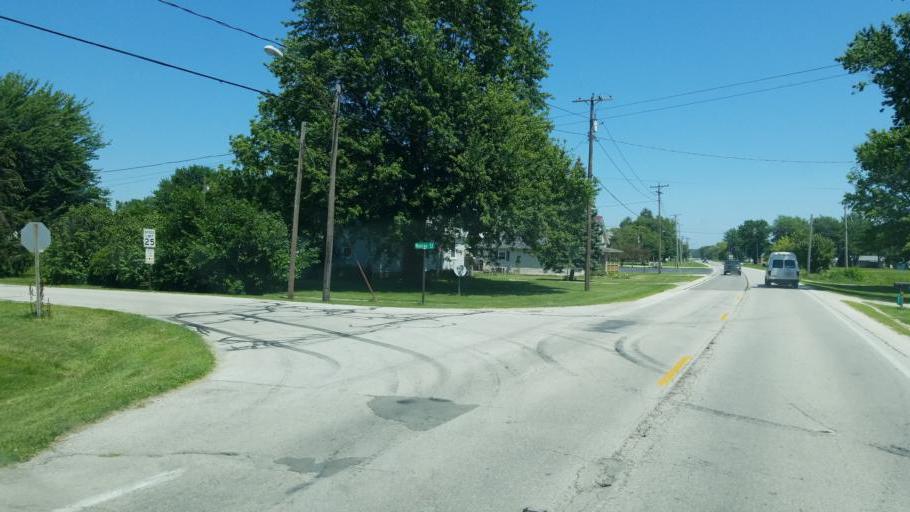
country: US
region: Ohio
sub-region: Ottawa County
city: Oak Harbor
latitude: 41.5158
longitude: -83.0439
